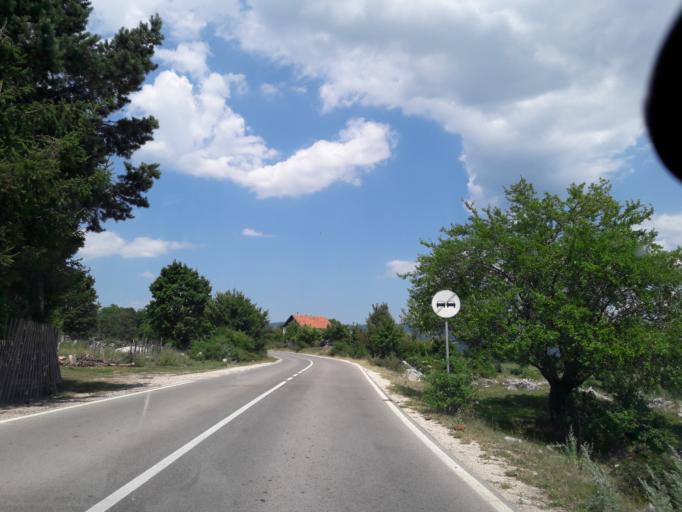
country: BA
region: Republika Srpska
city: Sipovo
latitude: 44.1677
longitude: 17.1674
